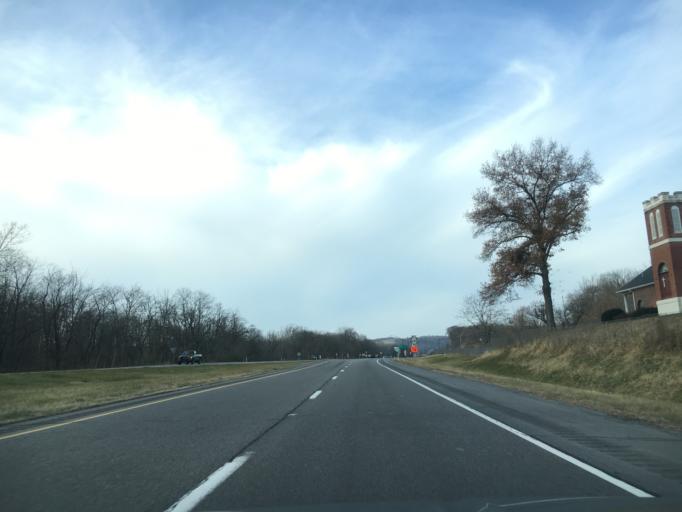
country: US
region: Pennsylvania
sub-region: Montour County
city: Danville
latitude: 40.9842
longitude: -76.6294
